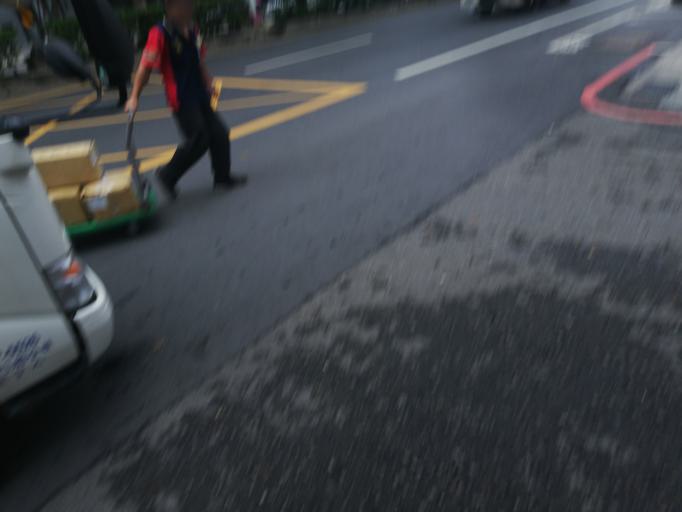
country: TW
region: Taiwan
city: Taoyuan City
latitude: 25.0111
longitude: 121.3009
